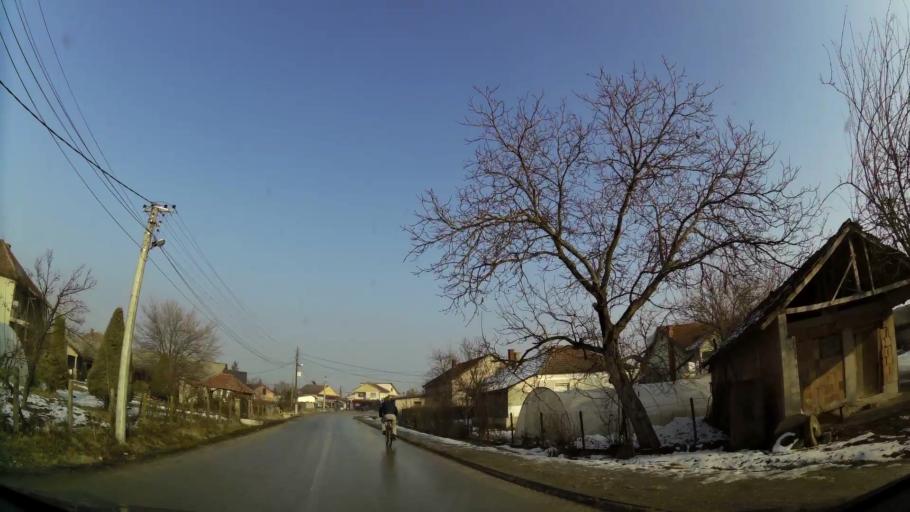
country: MK
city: Kadino
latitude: 41.9664
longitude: 21.5986
